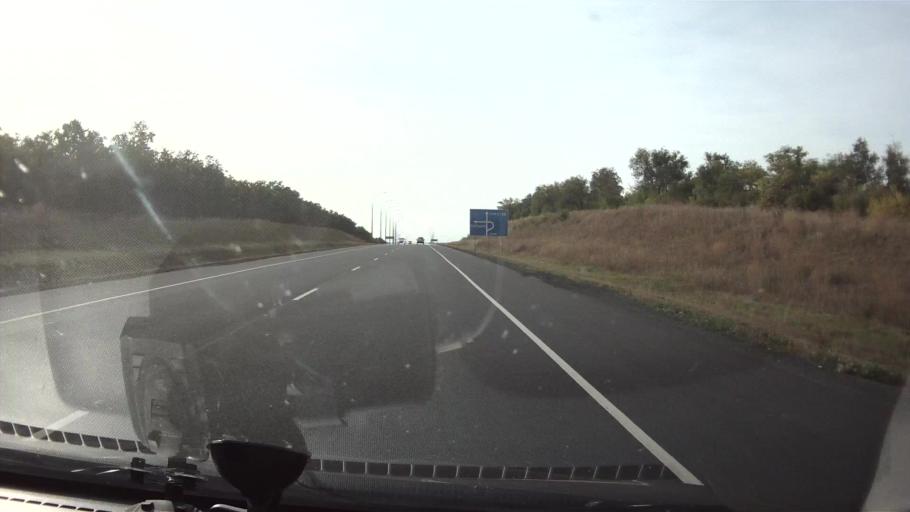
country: RU
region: Saratov
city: Yelshanka
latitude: 51.8250
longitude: 46.3071
